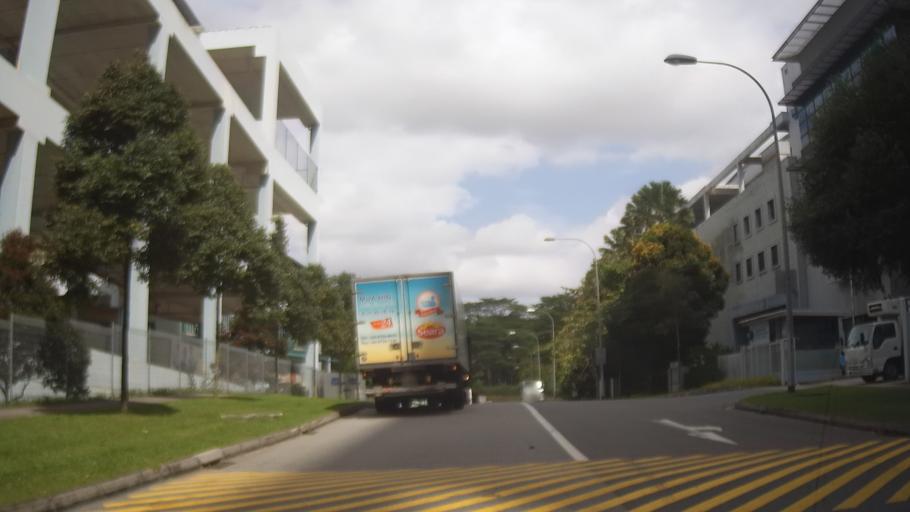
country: MY
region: Johor
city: Johor Bahru
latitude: 1.4097
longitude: 103.7578
